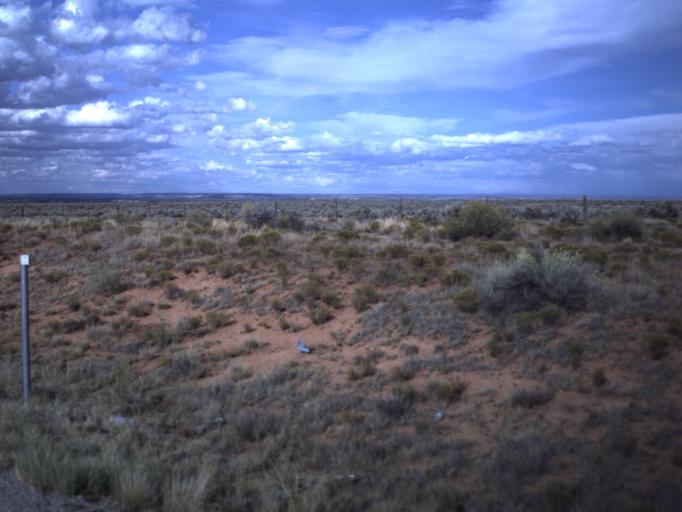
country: US
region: Utah
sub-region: San Juan County
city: Blanding
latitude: 37.3649
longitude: -109.3445
